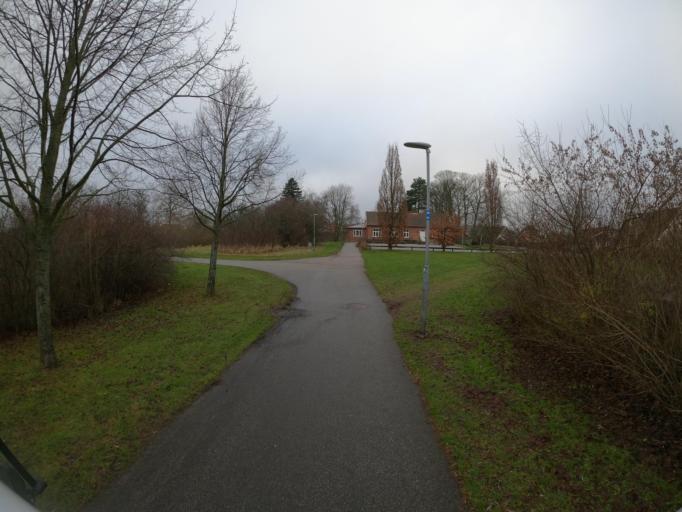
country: SE
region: Skane
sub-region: Svedala Kommun
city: Svedala
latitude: 55.5202
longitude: 13.2256
